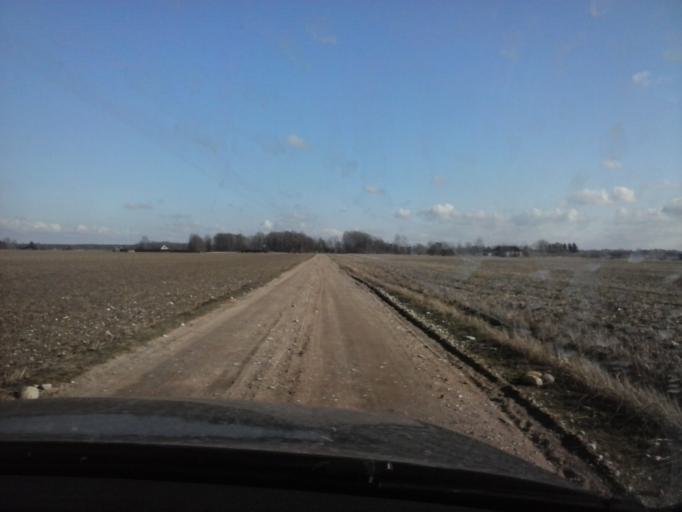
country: EE
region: Tartu
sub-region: Puhja vald
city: Puhja
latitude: 58.2849
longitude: 26.1532
